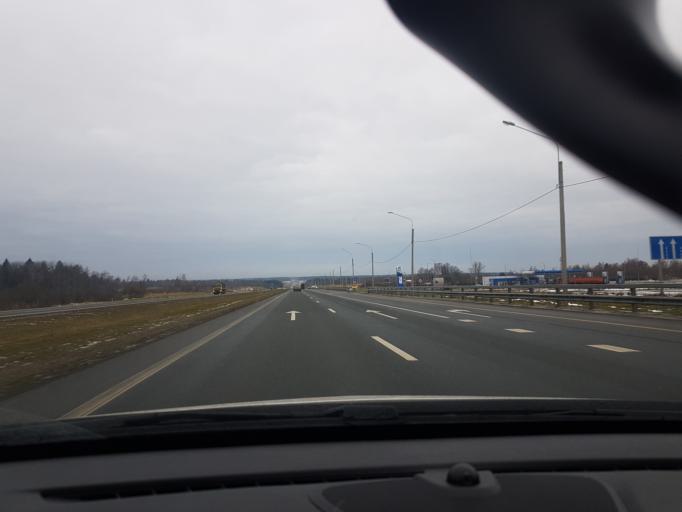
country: RU
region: Moskovskaya
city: Sychevo
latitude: 55.9895
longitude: 36.2734
